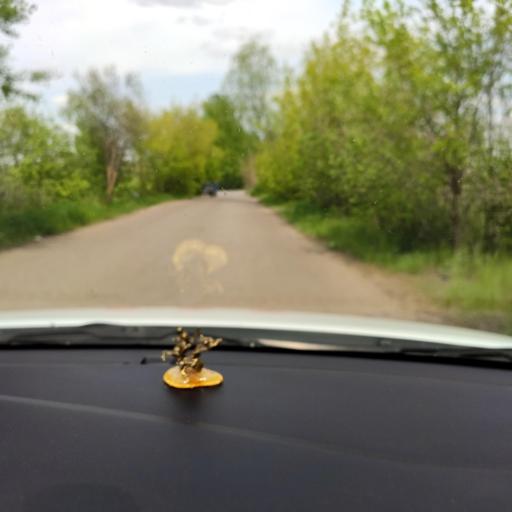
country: RU
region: Tatarstan
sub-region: Gorod Kazan'
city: Kazan
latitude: 55.6998
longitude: 49.0629
